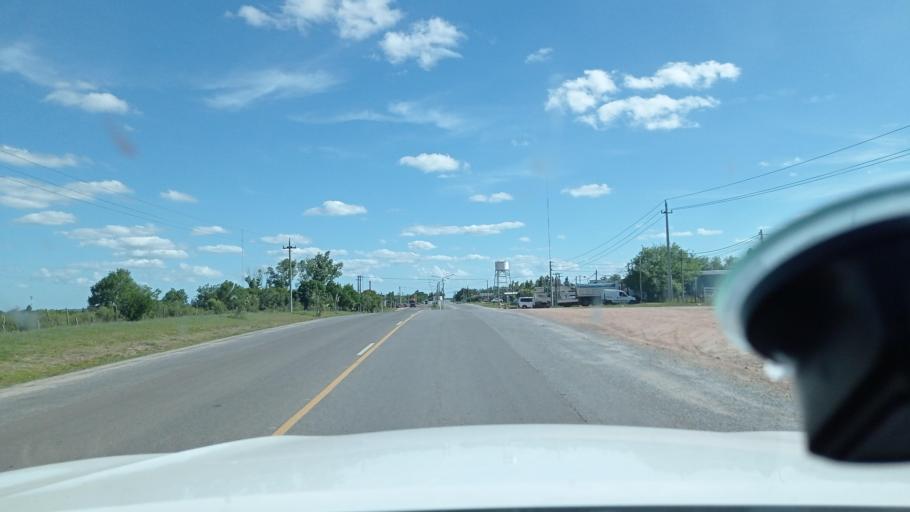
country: UY
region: Florida
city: Florida
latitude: -34.0839
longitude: -56.2366
